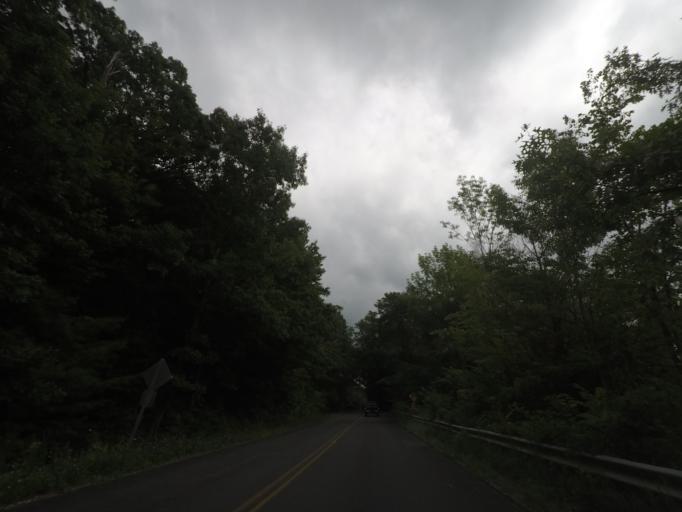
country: US
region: New York
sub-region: Rensselaer County
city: Poestenkill
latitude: 42.8376
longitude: -73.5238
